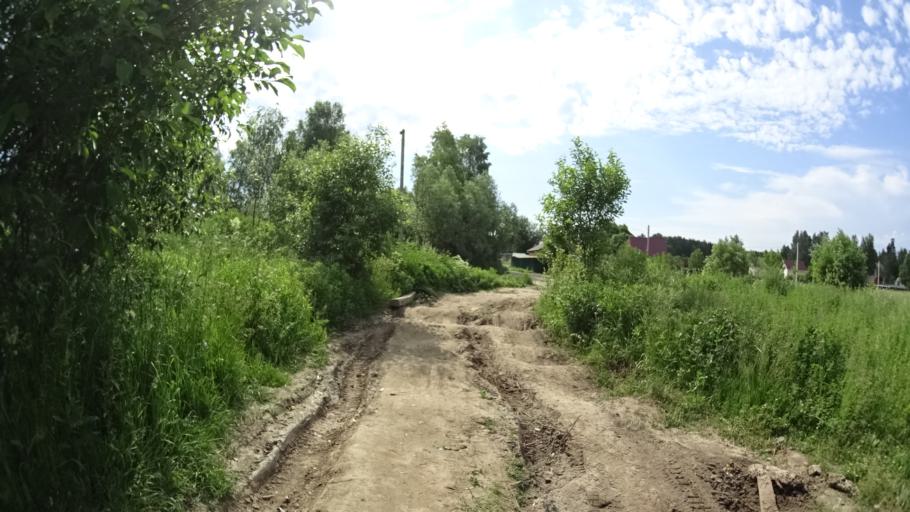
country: RU
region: Moskovskaya
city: Lesnoy
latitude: 56.0813
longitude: 37.9137
